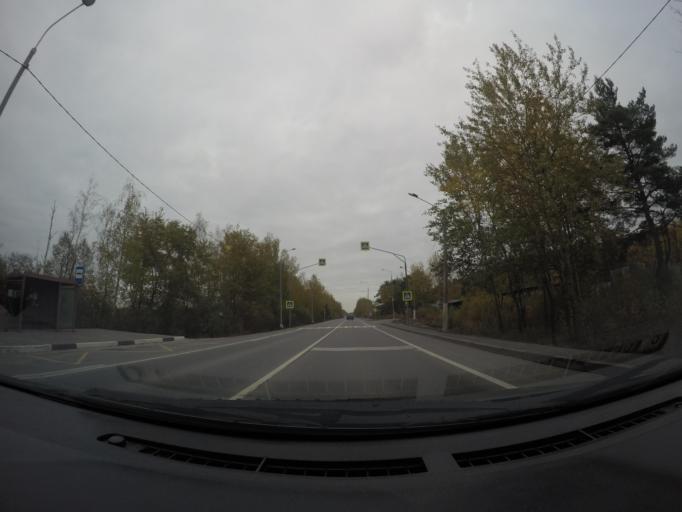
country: RU
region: Moskovskaya
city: Imeni Vorovskogo
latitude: 55.7219
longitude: 38.3756
